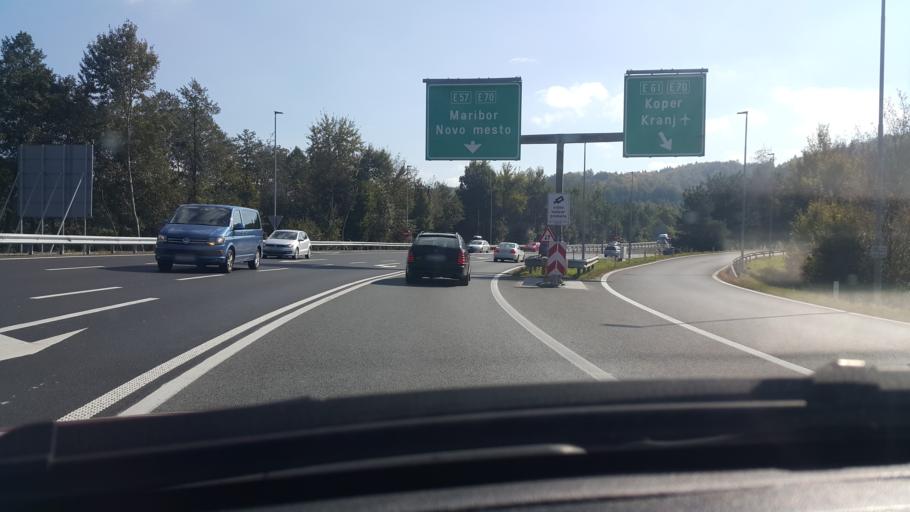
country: SI
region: Skofljica
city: Lavrica
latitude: 46.0160
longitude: 14.5453
